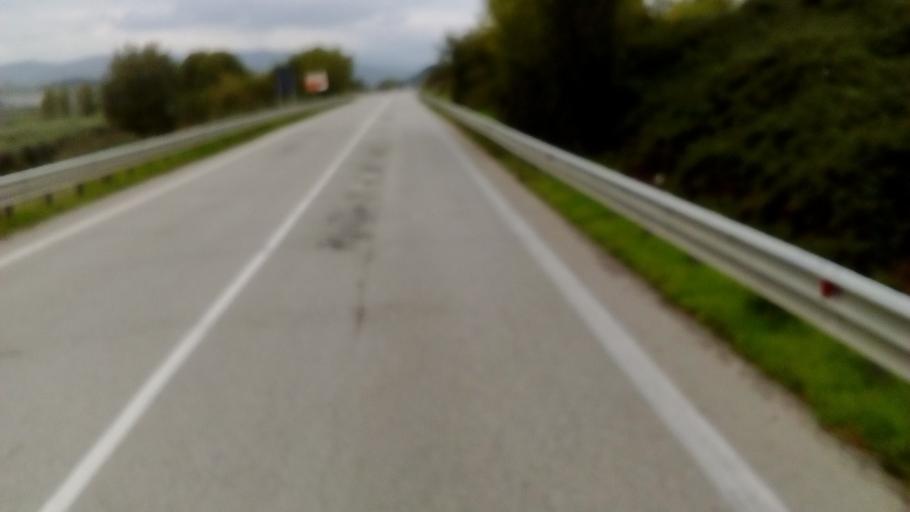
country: IT
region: Abruzzo
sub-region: Provincia di Chieti
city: San Salvo
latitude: 42.0197
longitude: 14.7296
